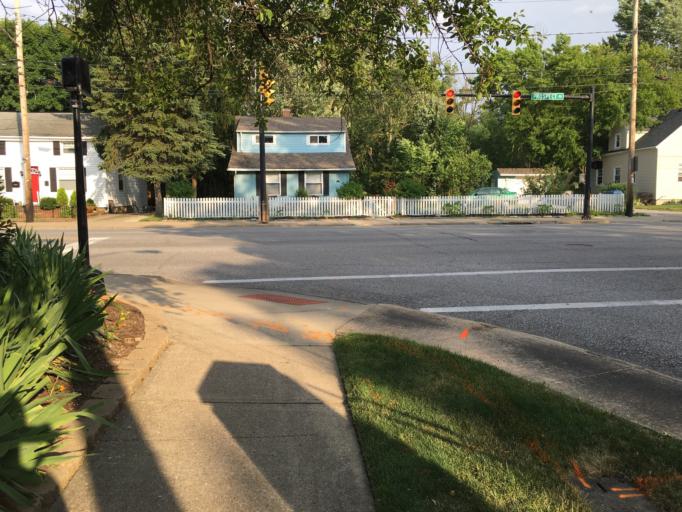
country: US
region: Ohio
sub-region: Cuyahoga County
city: Berea
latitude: 41.3657
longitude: -81.8583
